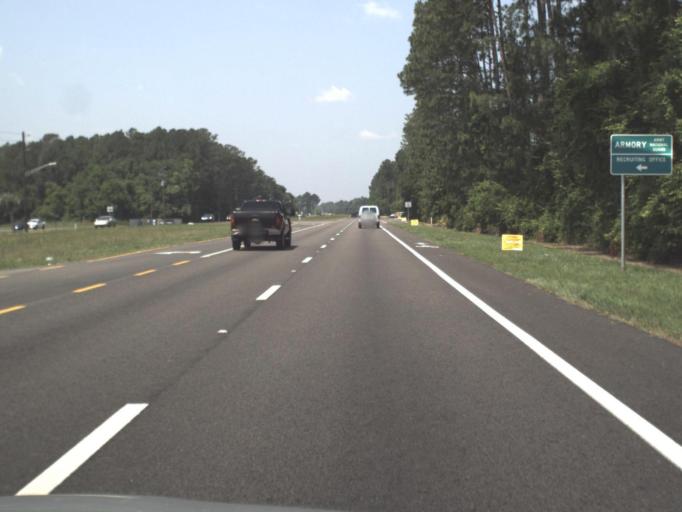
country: US
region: Florida
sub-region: Clay County
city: Bellair-Meadowbrook Terrace
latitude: 30.2794
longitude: -81.8209
